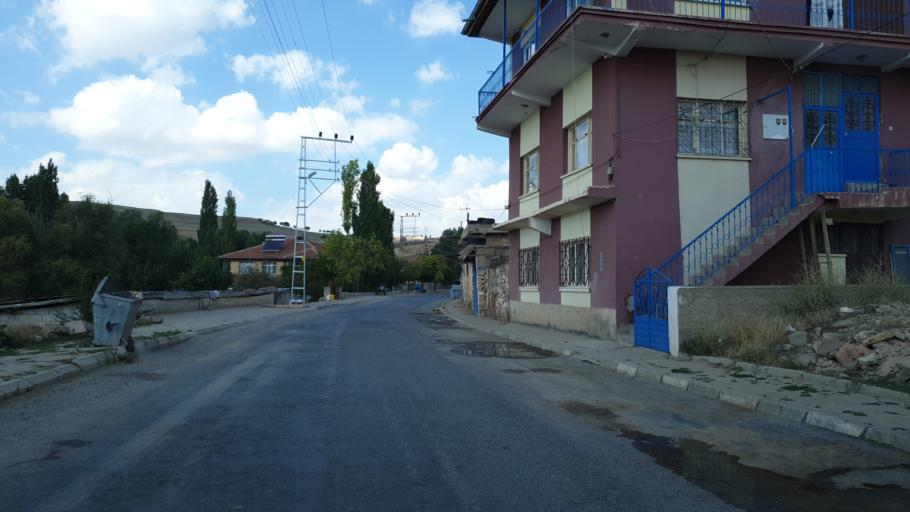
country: TR
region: Kayseri
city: Felahiye
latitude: 39.0925
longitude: 35.5631
